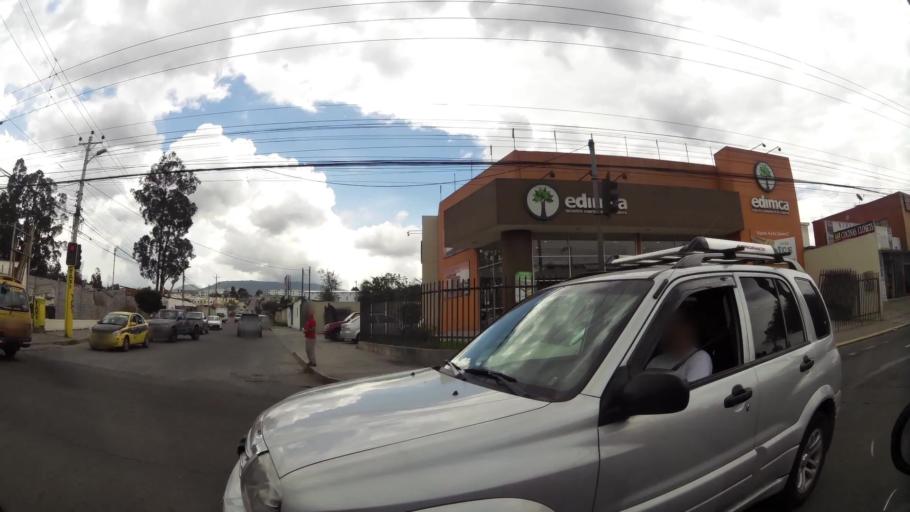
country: EC
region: Pichincha
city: Quito
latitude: -0.0892
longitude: -78.4280
